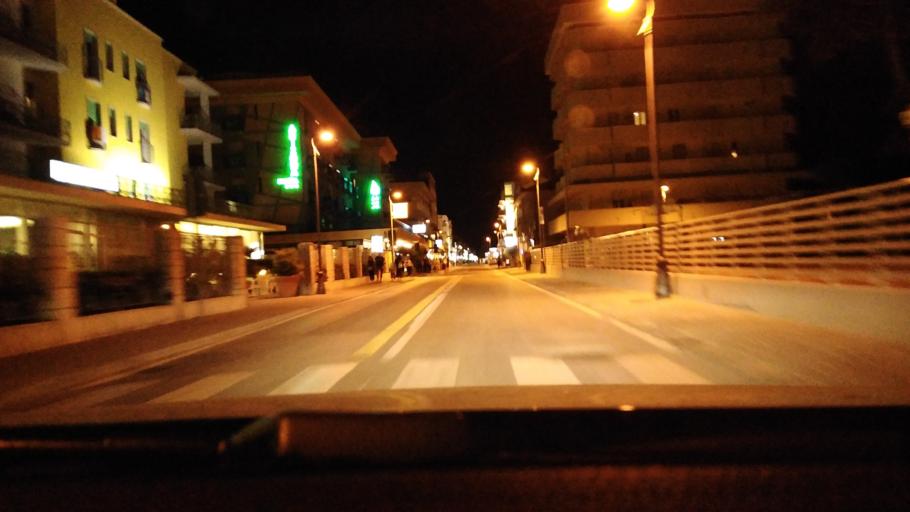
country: IT
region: Emilia-Romagna
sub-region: Provincia di Rimini
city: Bellaria-Igea Marina
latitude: 44.1320
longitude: 12.4850
